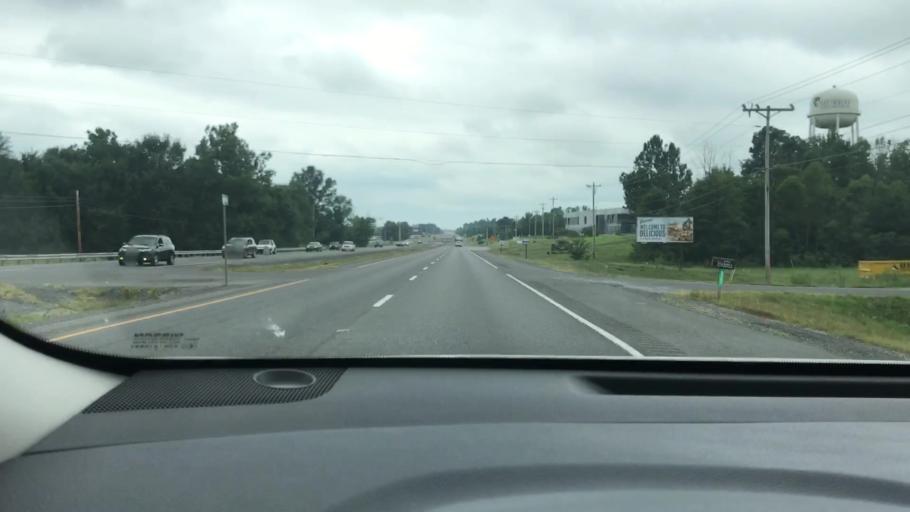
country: US
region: Kentucky
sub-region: Calloway County
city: Murray
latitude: 36.6639
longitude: -88.3051
